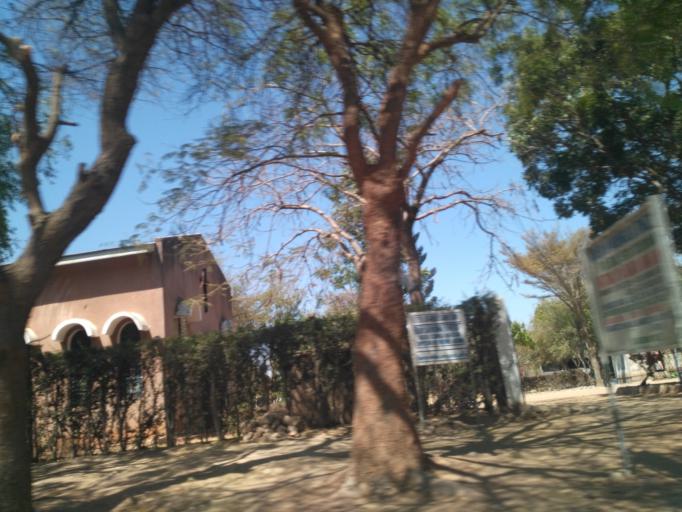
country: TZ
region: Dodoma
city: Dodoma
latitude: -6.1606
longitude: 35.7575
